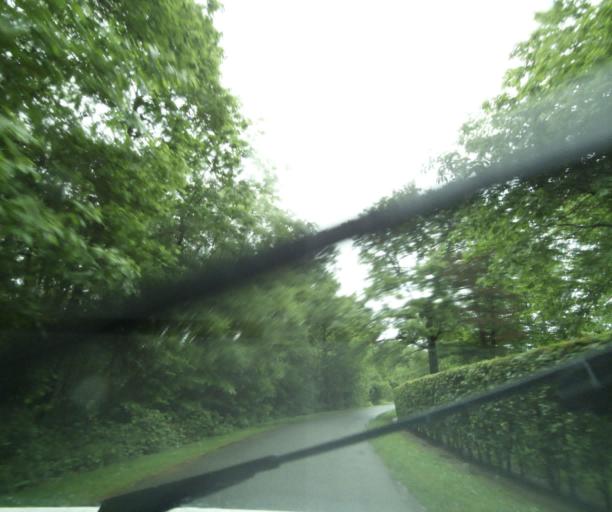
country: FR
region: Bourgogne
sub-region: Departement de Saone-et-Loire
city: Ciry-le-Noble
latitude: 46.5406
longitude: 4.3019
